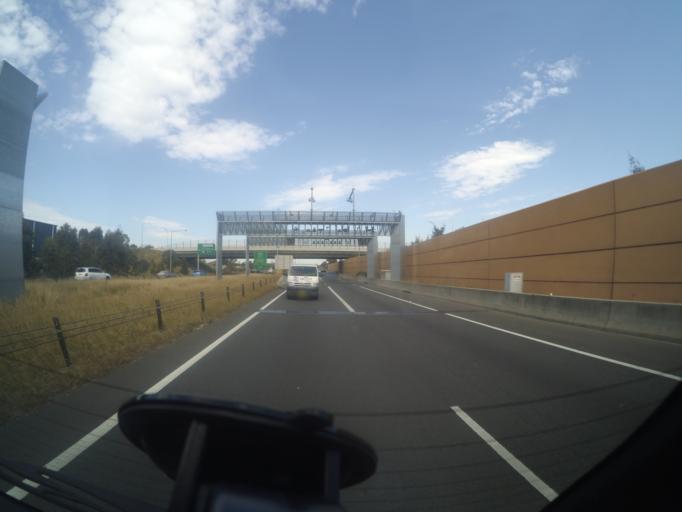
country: AU
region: New South Wales
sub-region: Liverpool
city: Miller
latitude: -33.9429
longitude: 150.8784
